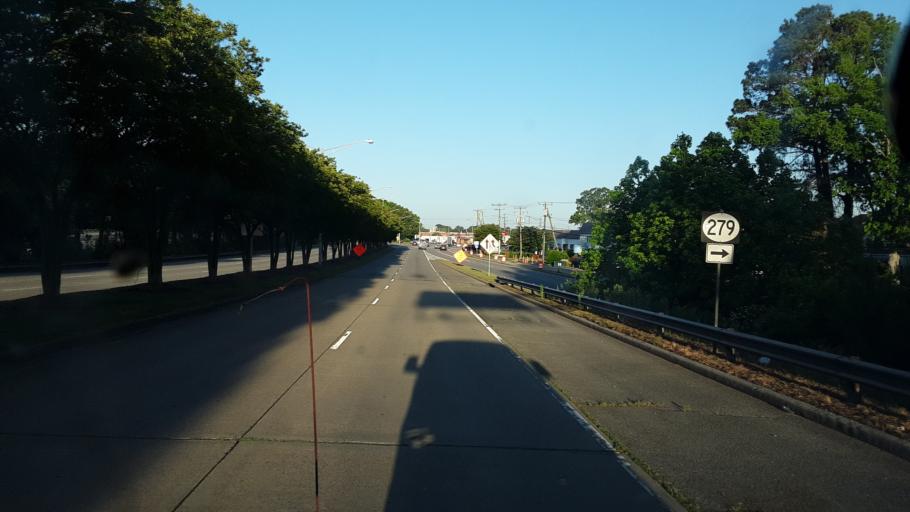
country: US
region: Virginia
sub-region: City of Virginia Beach
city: Virginia Beach
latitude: 36.8426
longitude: -76.0446
